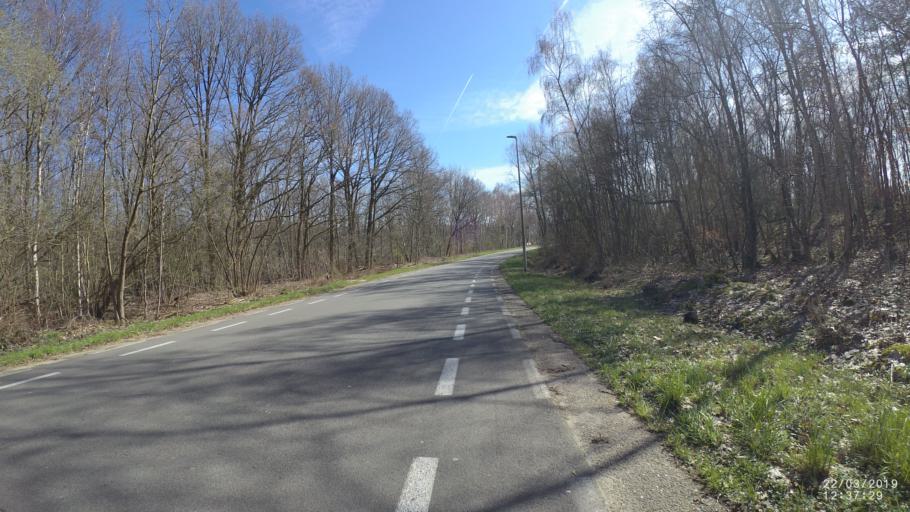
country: BE
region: Flanders
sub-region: Provincie Limburg
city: Zutendaal
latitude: 50.8873
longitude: 5.5735
